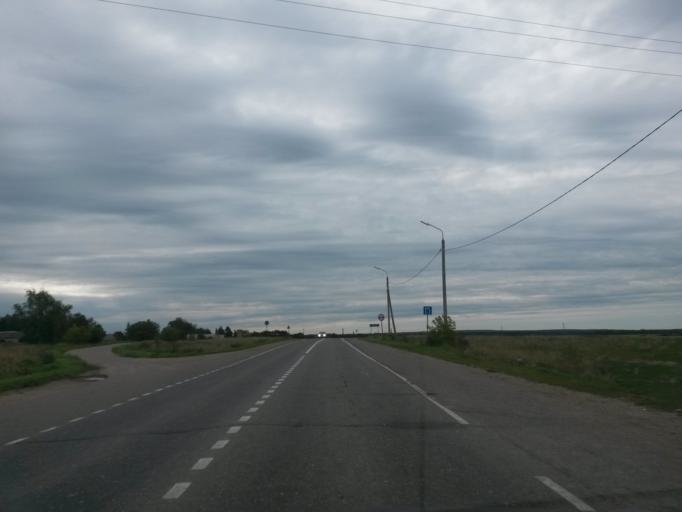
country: RU
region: Jaroslavl
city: Gavrilov-Yam
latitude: 57.3356
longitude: 39.8091
